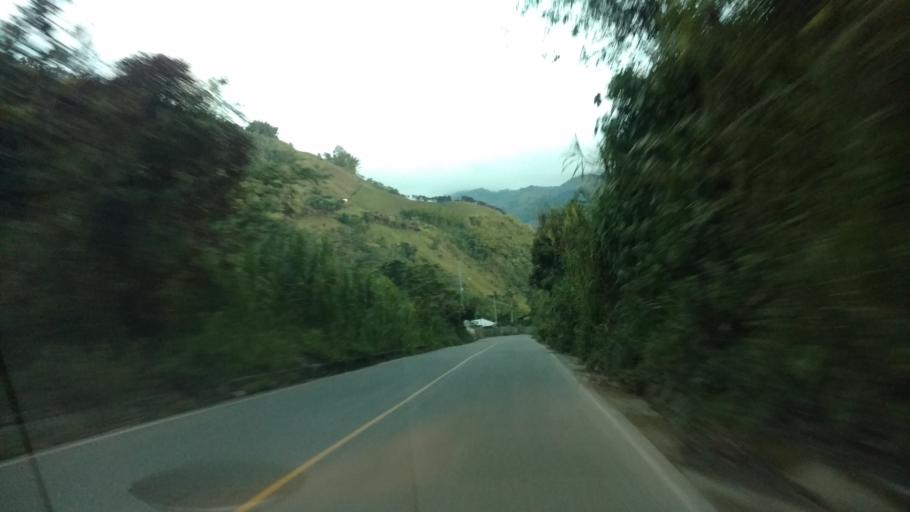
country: CO
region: Caldas
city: Aranzazu
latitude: 5.2620
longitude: -75.4993
